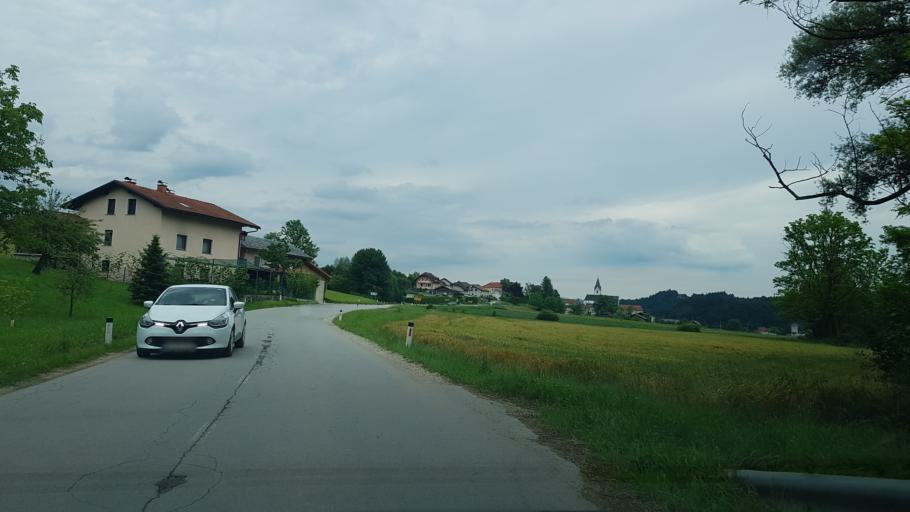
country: SI
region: Vojnik
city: Vojnik
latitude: 46.3188
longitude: 15.2812
